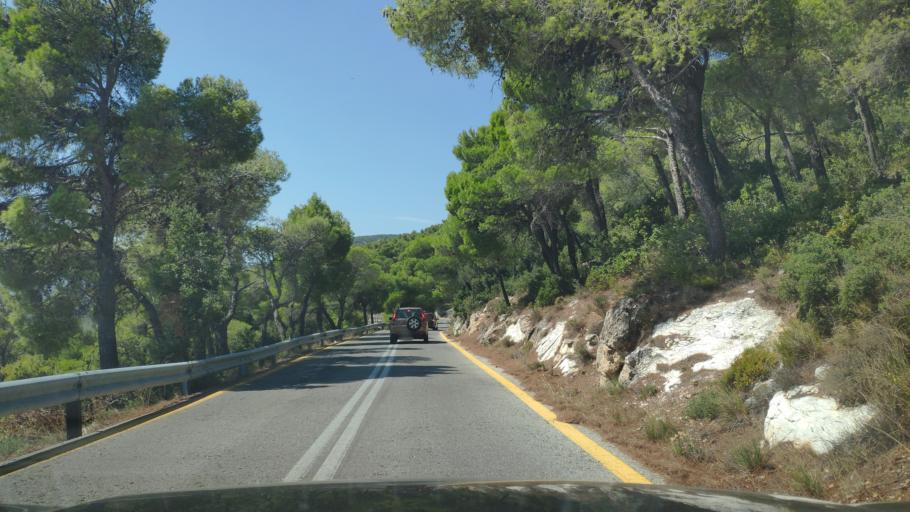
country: GR
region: Attica
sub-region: Nomarchia Anatolikis Attikis
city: Thrakomakedones
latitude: 38.1404
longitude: 23.7304
